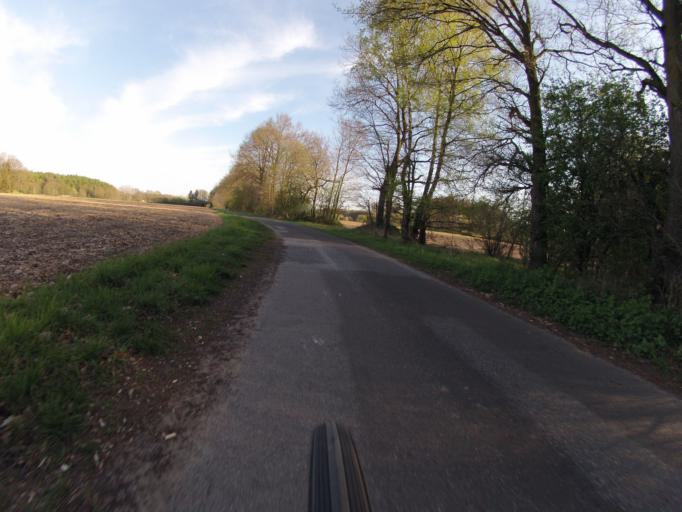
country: DE
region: Lower Saxony
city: Salzbergen
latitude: 52.3399
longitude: 7.3549
